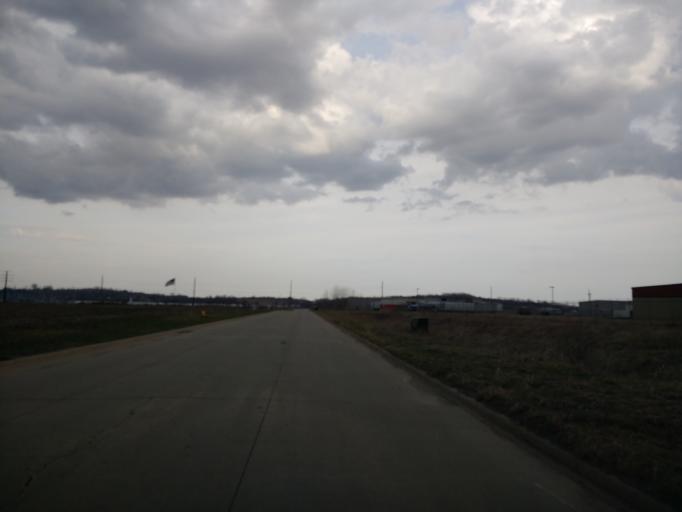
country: US
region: Iowa
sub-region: Woodbury County
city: Sergeant Bluff
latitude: 42.4148
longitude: -96.3754
